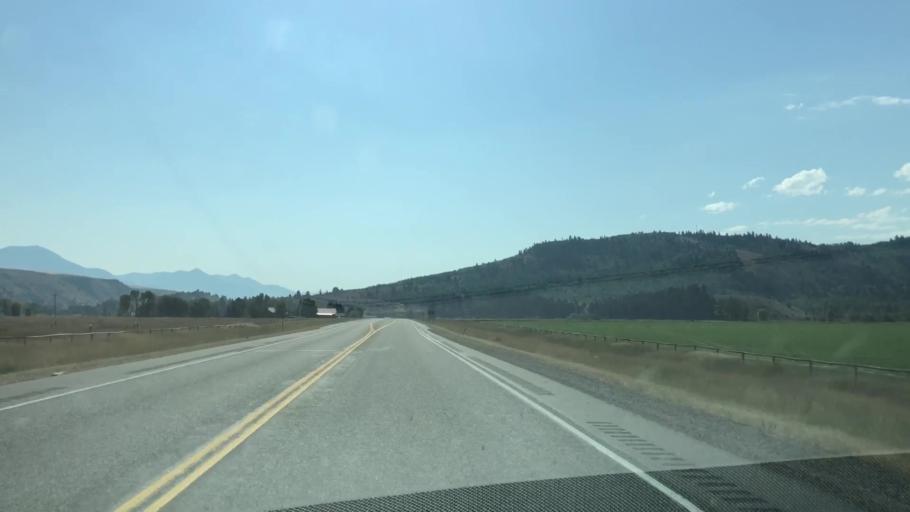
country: US
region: Idaho
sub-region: Teton County
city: Victor
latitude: 43.4636
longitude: -111.4336
